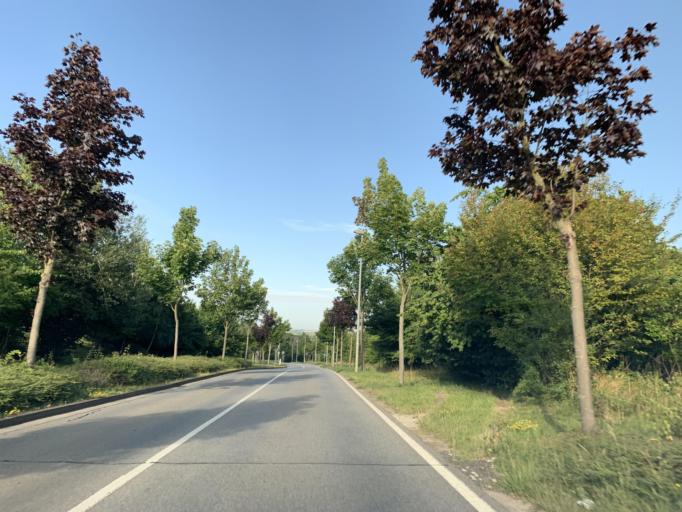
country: DE
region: Mecklenburg-Vorpommern
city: Trollenhagen
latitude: 53.5861
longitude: 13.2827
